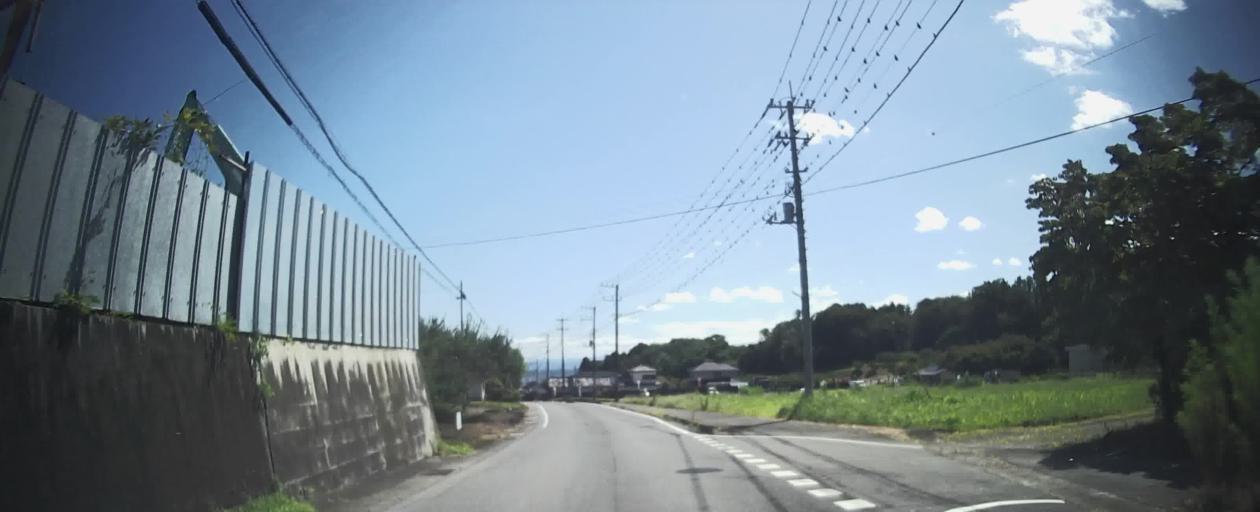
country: JP
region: Gunma
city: Kanekomachi
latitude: 36.4065
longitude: 138.9534
